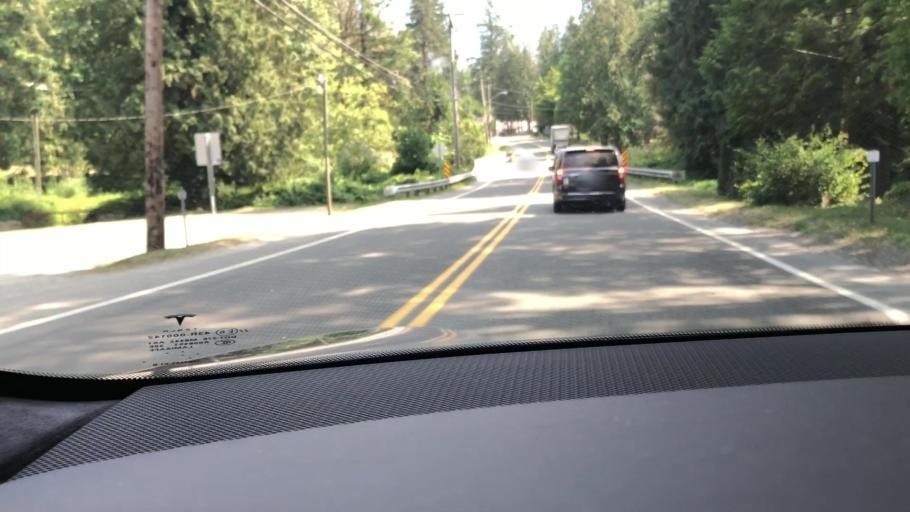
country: CA
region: British Columbia
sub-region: Fraser Valley Regional District
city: Chilliwack
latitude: 49.0778
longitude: -121.9797
